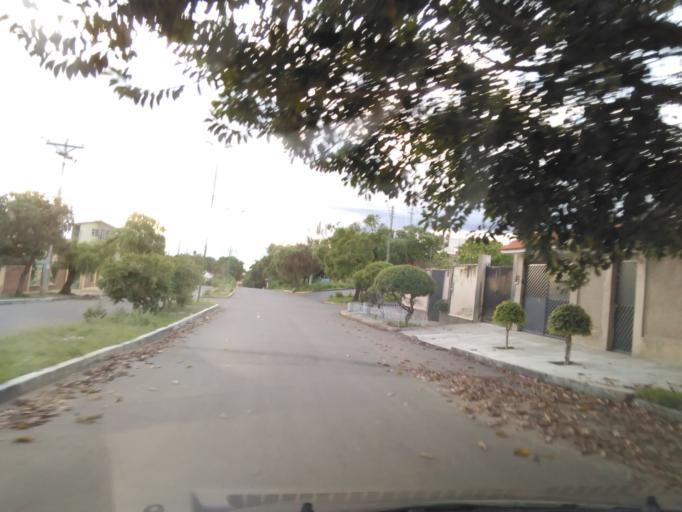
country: BO
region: Cochabamba
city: Cochabamba
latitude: -17.3538
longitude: -66.1558
